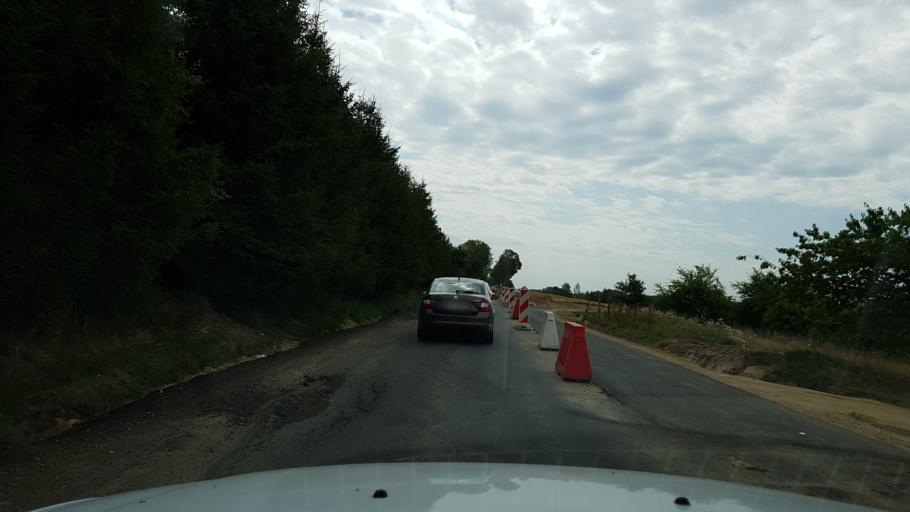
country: PL
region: West Pomeranian Voivodeship
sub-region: Powiat koszalinski
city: Mielno
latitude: 54.2013
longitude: 16.0119
